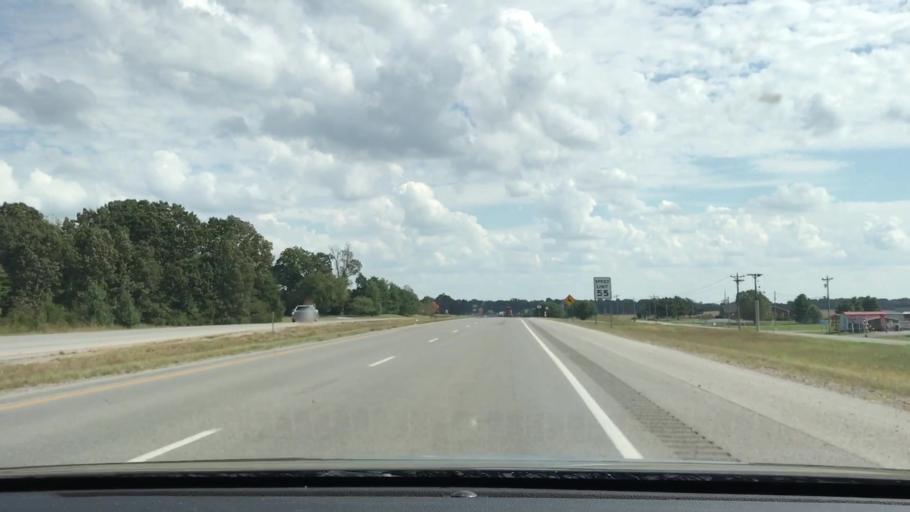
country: US
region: Kentucky
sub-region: Trigg County
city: Cadiz
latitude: 36.8676
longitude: -87.7911
